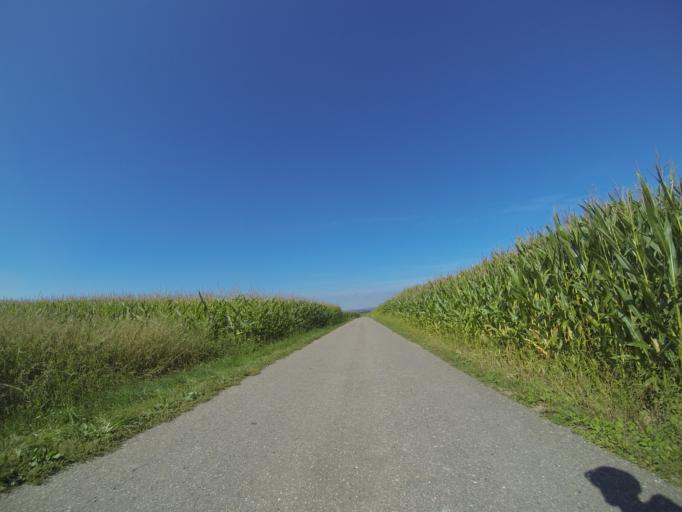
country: DE
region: Baden-Wuerttemberg
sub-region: Tuebingen Region
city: Achstetten
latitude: 48.2693
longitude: 9.9179
